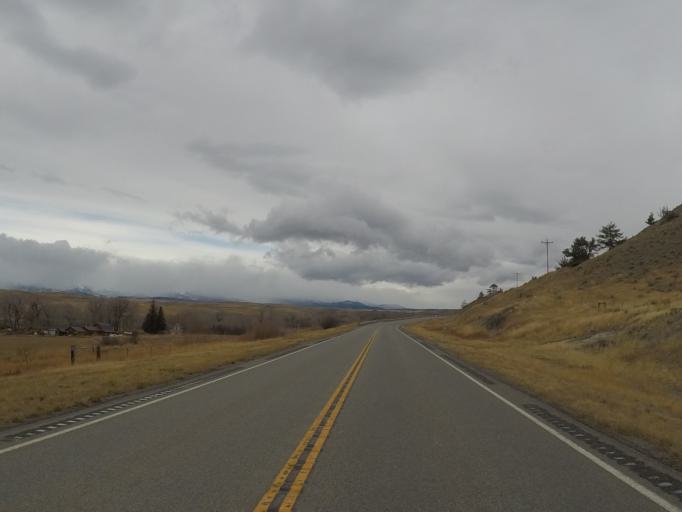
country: US
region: Montana
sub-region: Sweet Grass County
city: Big Timber
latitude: 45.8795
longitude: -109.9544
